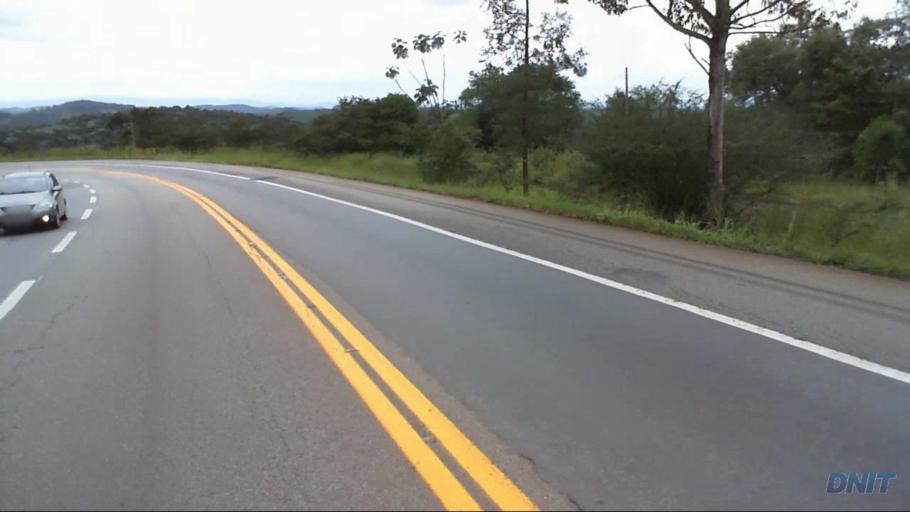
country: BR
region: Minas Gerais
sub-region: Caete
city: Caete
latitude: -19.7399
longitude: -43.5163
